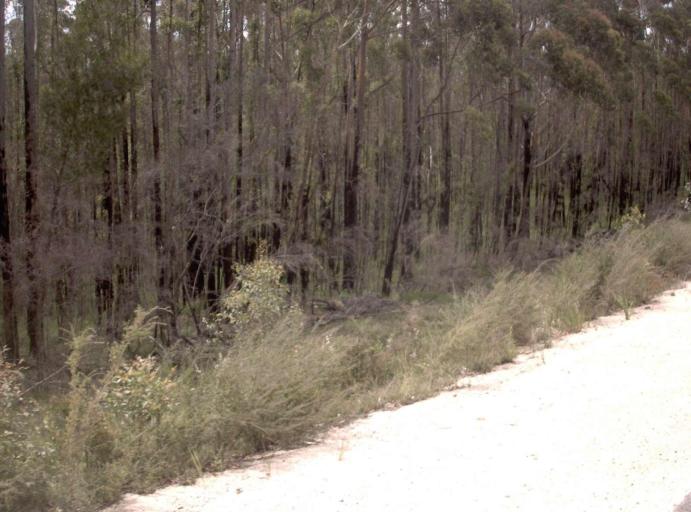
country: AU
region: New South Wales
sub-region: Bega Valley
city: Eden
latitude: -37.5329
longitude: 149.4849
